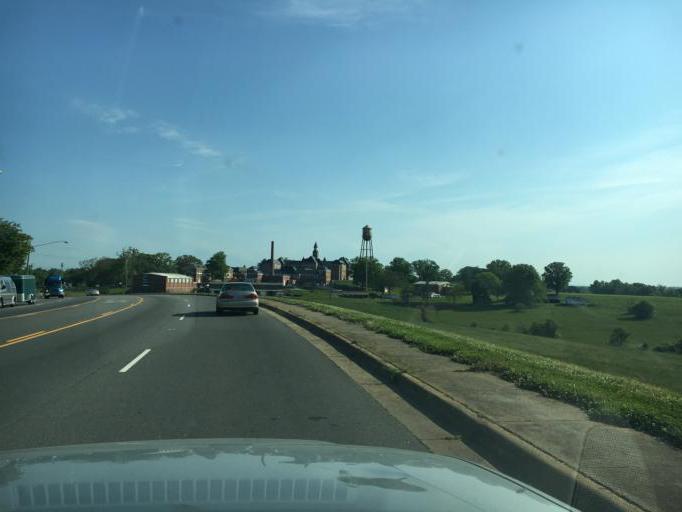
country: US
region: North Carolina
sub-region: Burke County
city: Morganton
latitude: 35.7248
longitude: -81.6926
